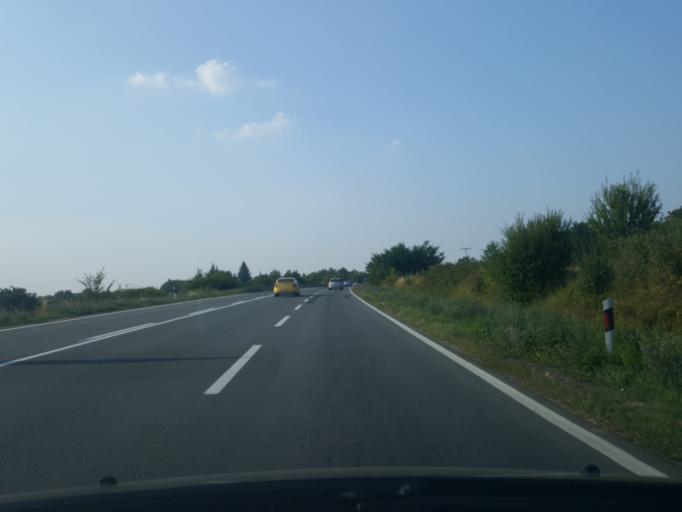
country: RS
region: Central Serbia
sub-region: Belgrade
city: Sopot
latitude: 44.5168
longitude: 20.6528
